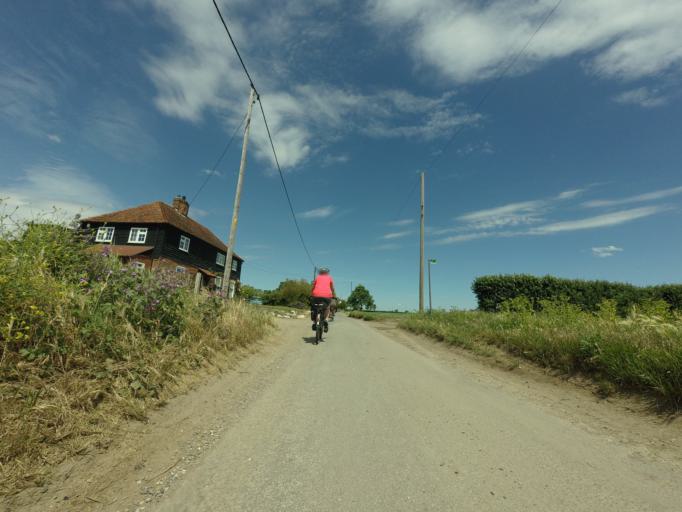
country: GB
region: England
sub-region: Kent
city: Cliffe
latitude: 51.4587
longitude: 0.4906
